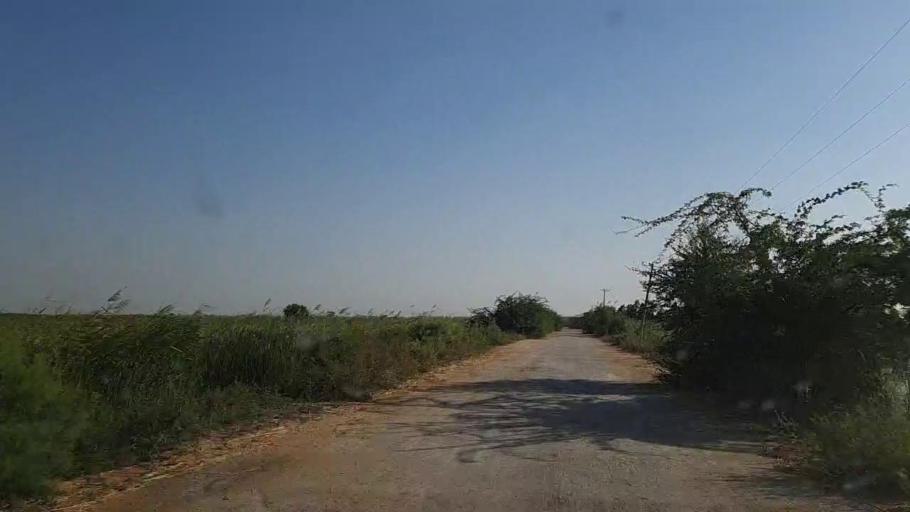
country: PK
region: Sindh
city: Thatta
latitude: 24.6399
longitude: 68.0757
